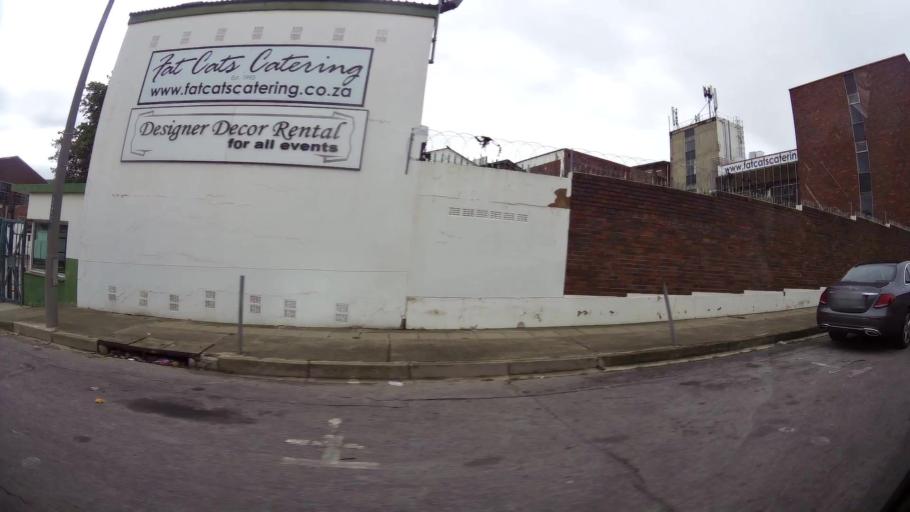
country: ZA
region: Eastern Cape
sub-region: Nelson Mandela Bay Metropolitan Municipality
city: Port Elizabeth
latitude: -33.9536
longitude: 25.6119
